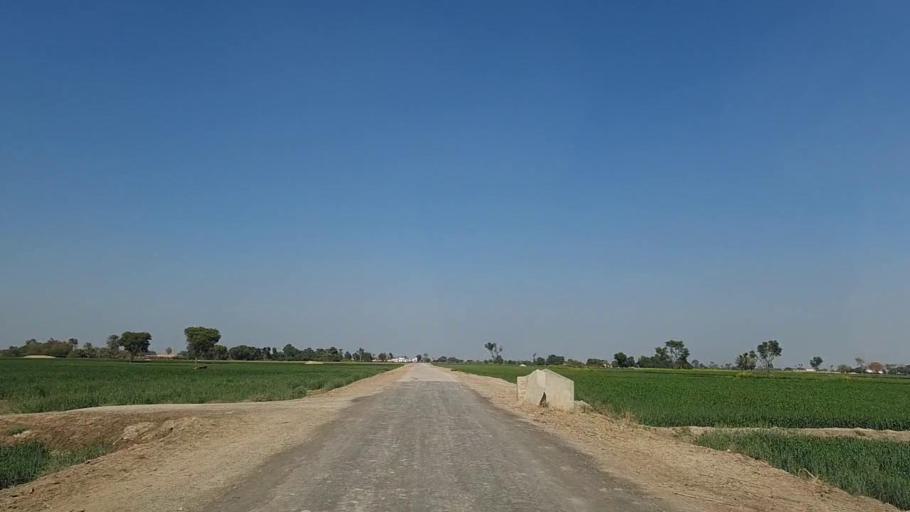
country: PK
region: Sindh
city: Nawabshah
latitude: 26.2530
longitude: 68.4514
